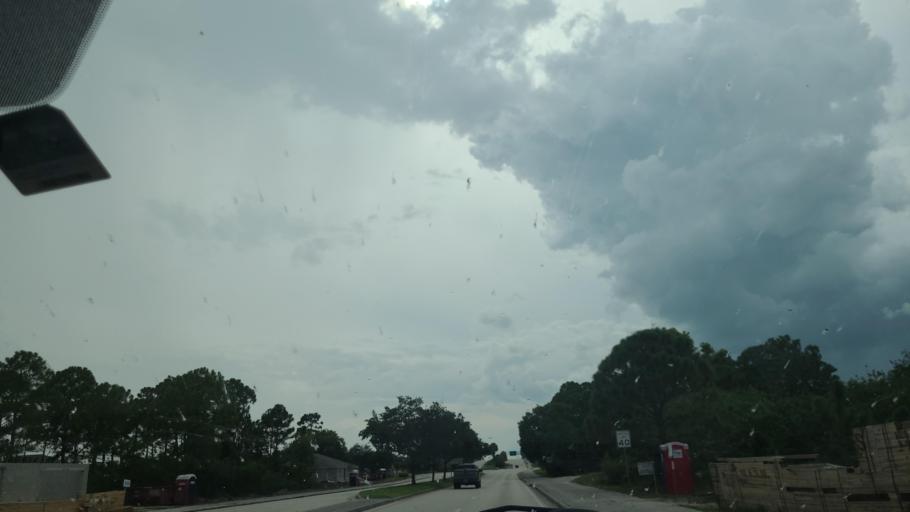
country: US
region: Florida
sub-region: Saint Lucie County
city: Port Saint Lucie
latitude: 27.2098
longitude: -80.3926
